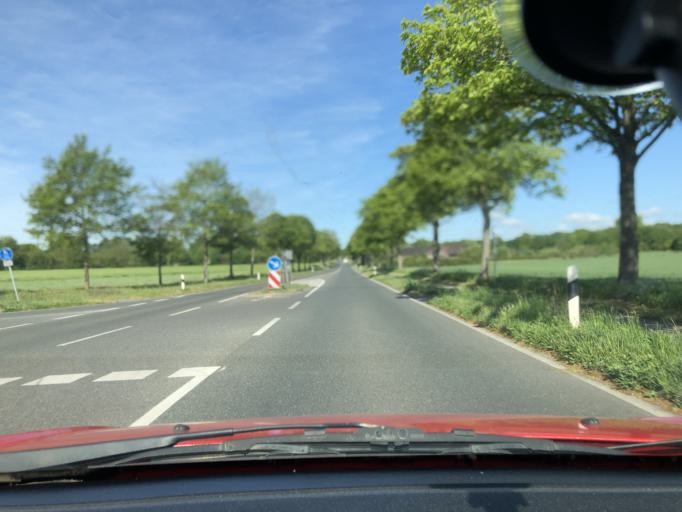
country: DE
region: North Rhine-Westphalia
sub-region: Regierungsbezirk Dusseldorf
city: Moers
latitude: 51.4921
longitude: 6.6189
